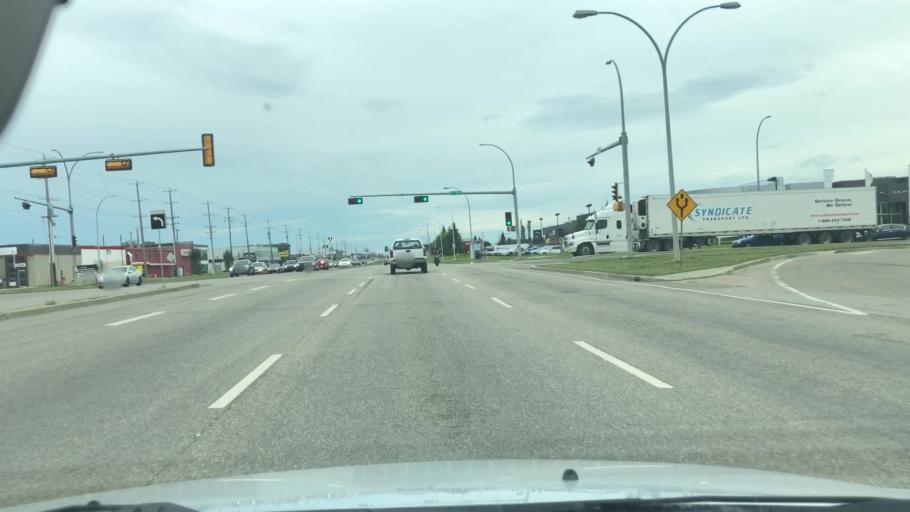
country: CA
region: Alberta
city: St. Albert
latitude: 53.5600
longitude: -113.6154
